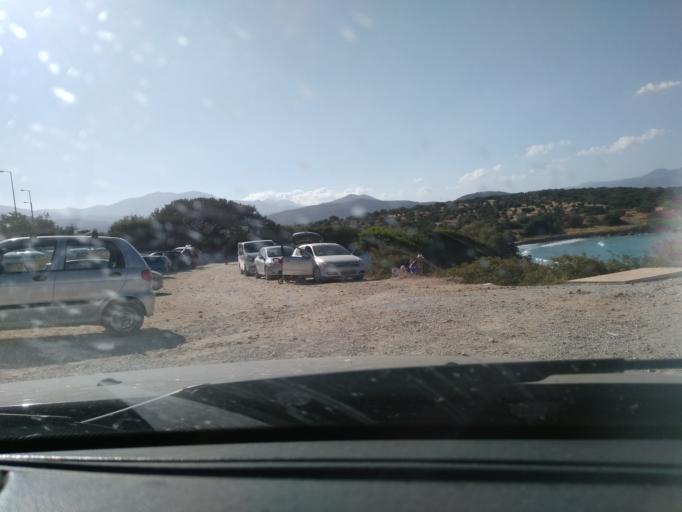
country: GR
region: Crete
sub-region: Nomos Lasithiou
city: Agios Nikolaos
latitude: 35.1252
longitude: 25.7429
